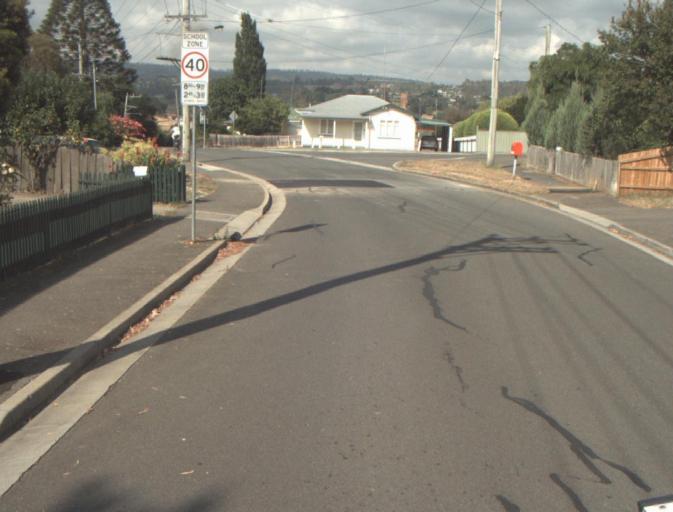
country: AU
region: Tasmania
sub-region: Launceston
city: Newstead
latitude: -41.4601
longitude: 147.1979
